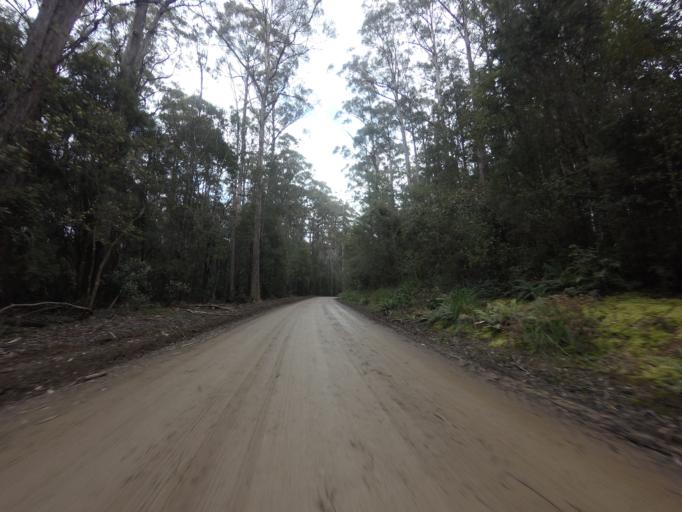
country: AU
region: Tasmania
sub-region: Huon Valley
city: Geeveston
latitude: -43.4164
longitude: 146.8877
